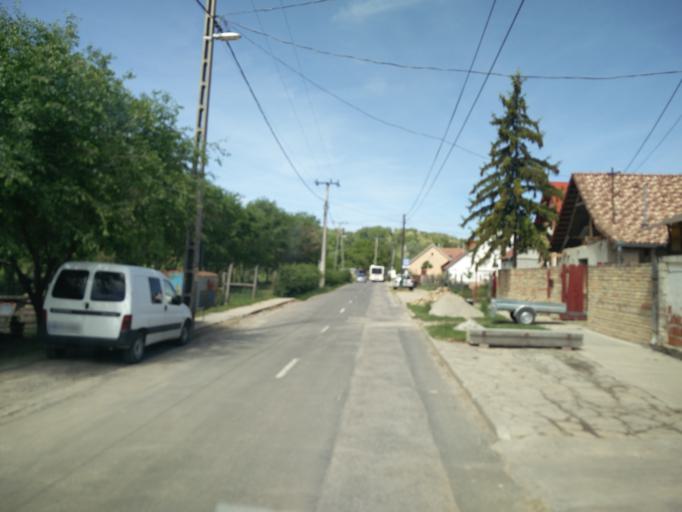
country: HU
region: Tolna
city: Szekszard
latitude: 46.3090
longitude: 18.6868
